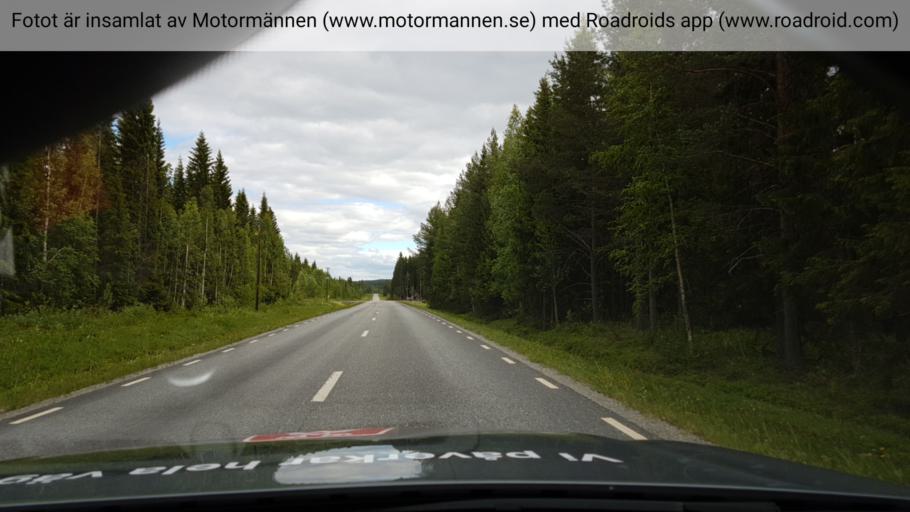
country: SE
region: Jaemtland
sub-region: Stroemsunds Kommun
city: Stroemsund
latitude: 63.9326
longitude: 15.4984
